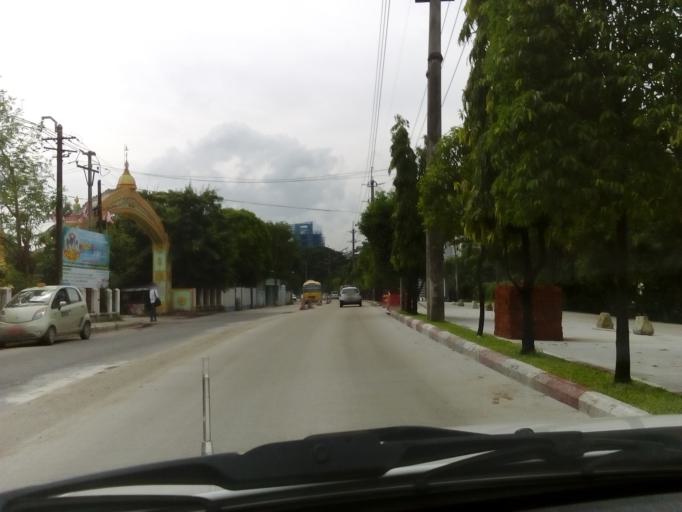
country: MM
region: Yangon
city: Yangon
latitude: 16.8651
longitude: 96.1401
